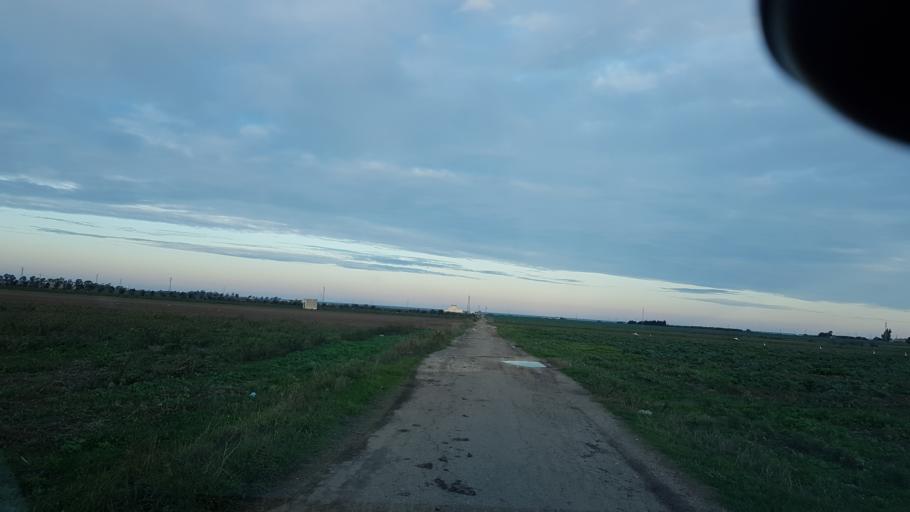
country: IT
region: Apulia
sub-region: Provincia di Brindisi
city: La Rosa
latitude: 40.5990
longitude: 17.9955
